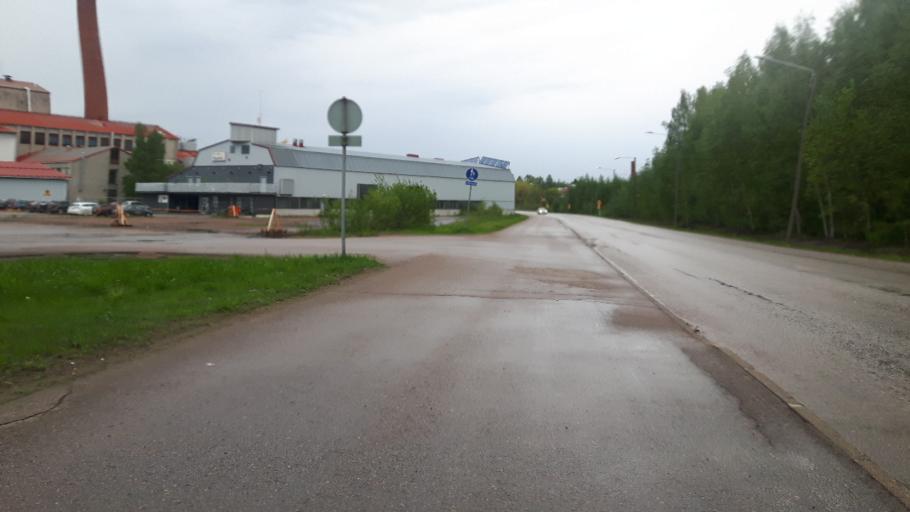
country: FI
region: Kymenlaakso
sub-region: Kotka-Hamina
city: Kotka
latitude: 60.4989
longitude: 26.9035
